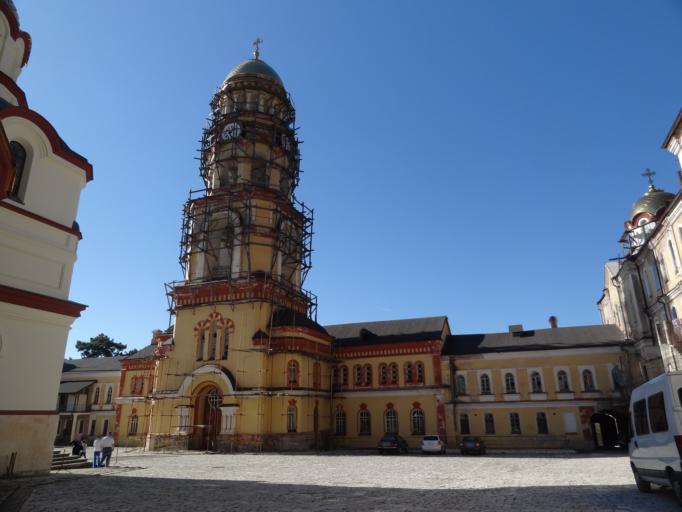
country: GE
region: Abkhazia
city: Stantsiya Novyy Afon
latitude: 43.0883
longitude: 40.8209
